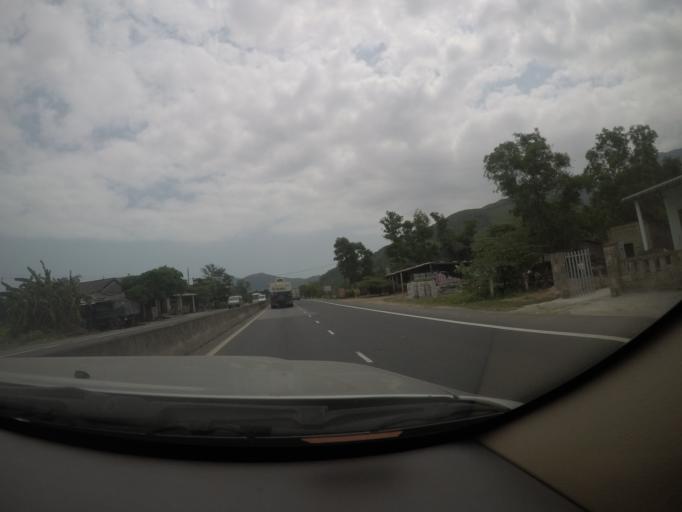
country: VN
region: Thua Thien-Hue
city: Phu Loc
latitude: 16.2708
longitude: 108.0062
